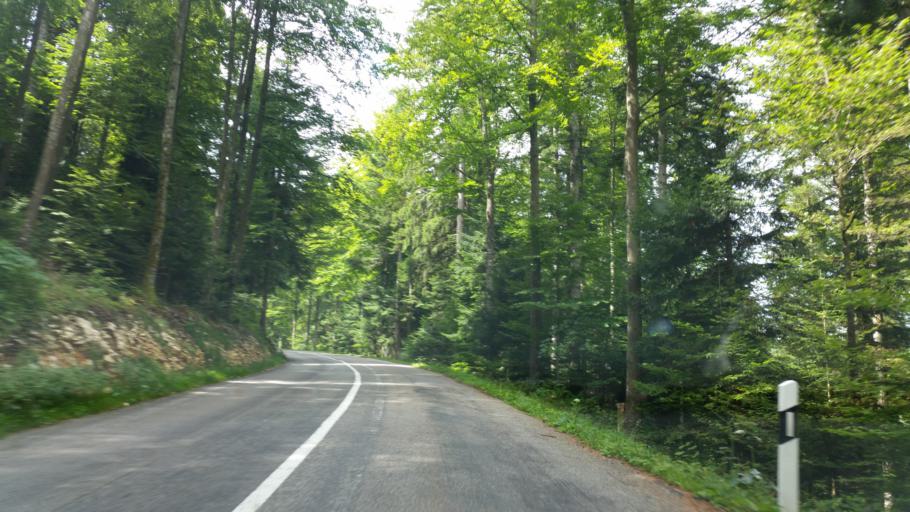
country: CH
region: Neuchatel
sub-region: La Chaux-de-Fonds District
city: La Chaux-de-Fonds
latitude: 47.1282
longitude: 6.8255
